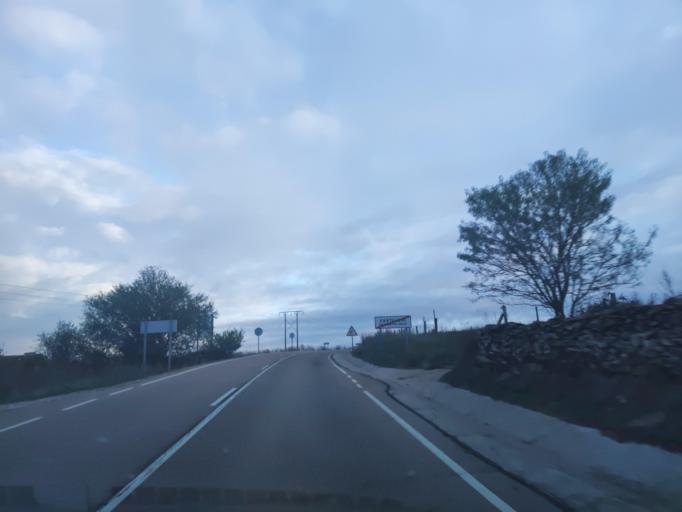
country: ES
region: Castille and Leon
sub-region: Provincia de Salamanca
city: Castillejo de Martin Viejo
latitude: 40.7019
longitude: -6.6481
